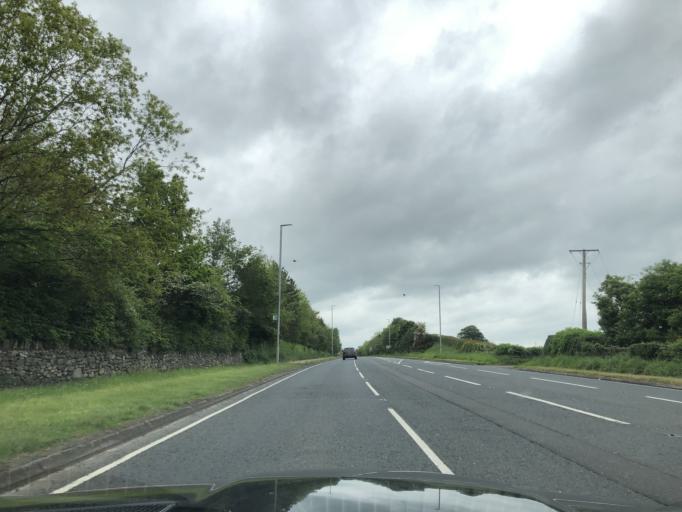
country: GB
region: Northern Ireland
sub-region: Down District
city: Downpatrick
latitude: 54.3450
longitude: -5.7335
